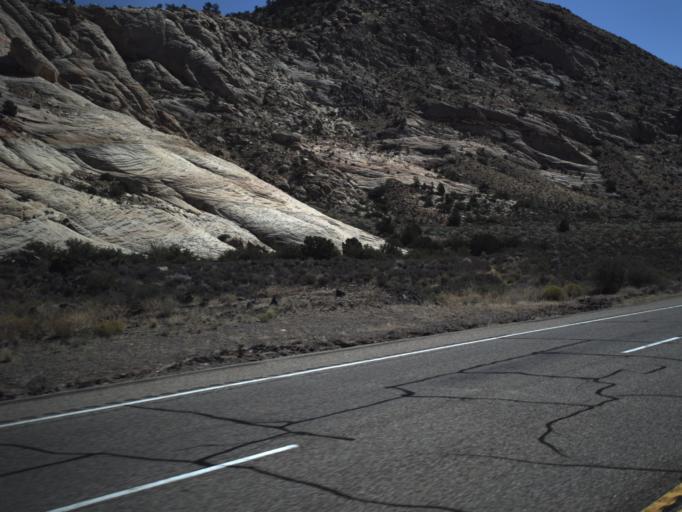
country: US
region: Utah
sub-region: Washington County
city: Ivins
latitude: 37.2367
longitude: -113.6357
